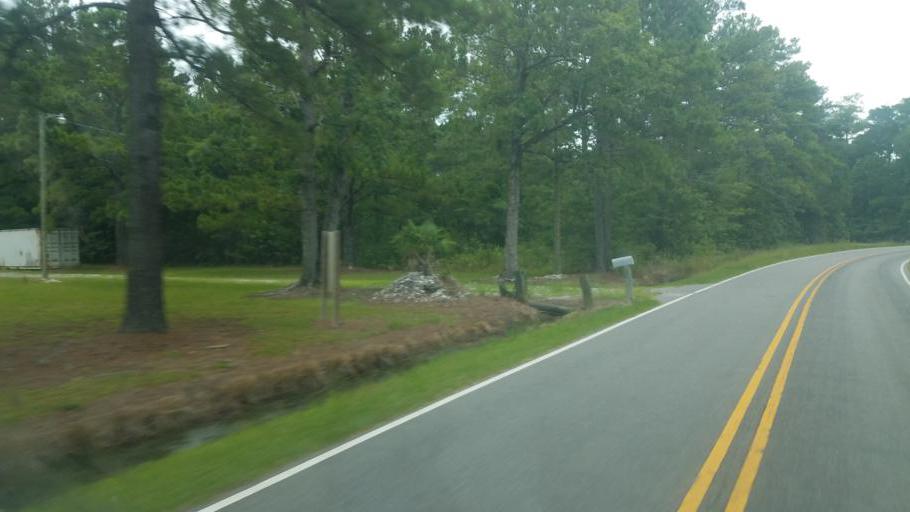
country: US
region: North Carolina
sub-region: Tyrrell County
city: Columbia
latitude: 35.9482
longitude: -76.2889
